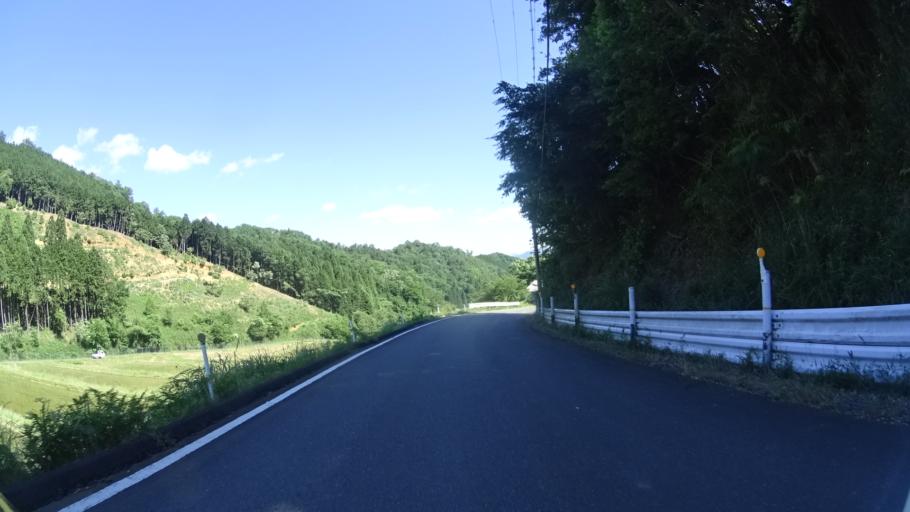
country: JP
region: Kyoto
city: Fukuchiyama
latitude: 35.3892
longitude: 135.0715
